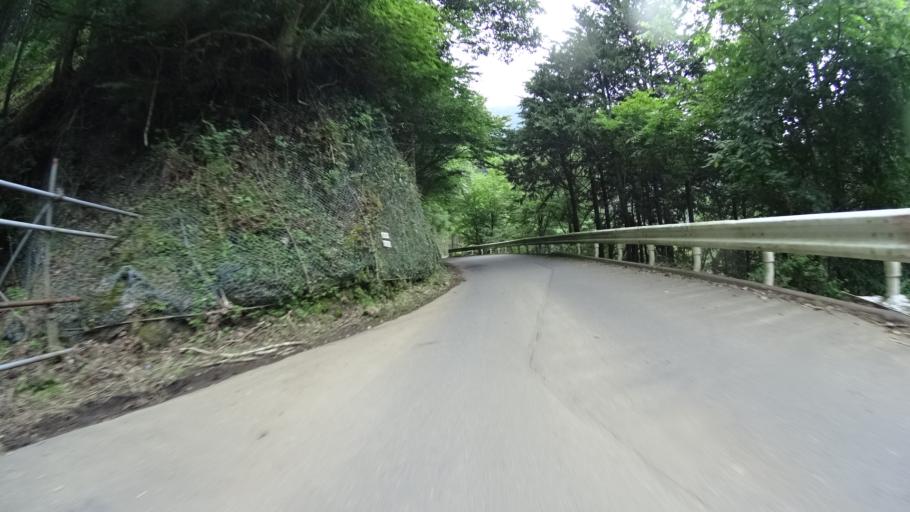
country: JP
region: Kanagawa
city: Hadano
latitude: 35.4897
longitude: 139.2210
